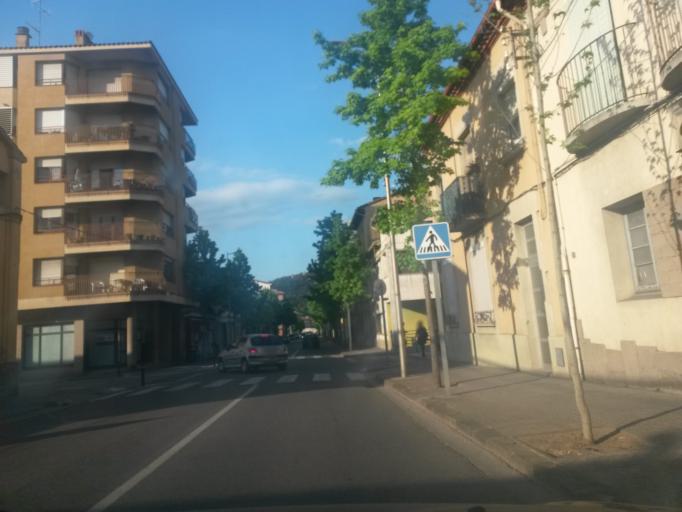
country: ES
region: Catalonia
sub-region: Provincia de Girona
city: Olot
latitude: 42.1862
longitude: 2.4957
